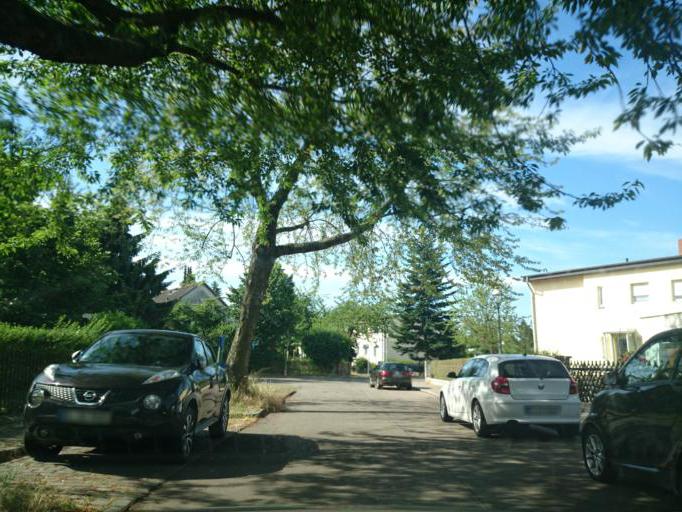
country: DE
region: Brandenburg
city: Teltow
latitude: 52.4230
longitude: 13.2773
